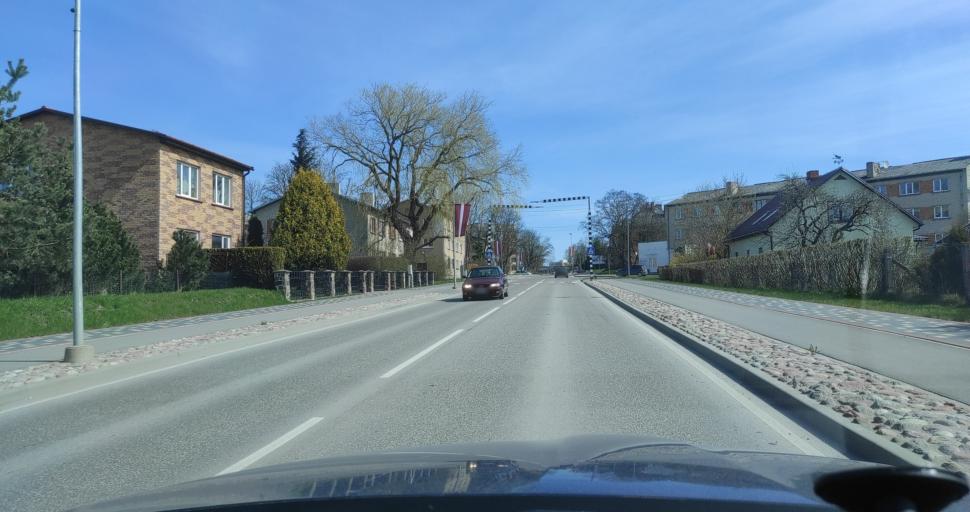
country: LV
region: Talsu Rajons
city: Talsi
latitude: 57.2408
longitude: 22.5783
